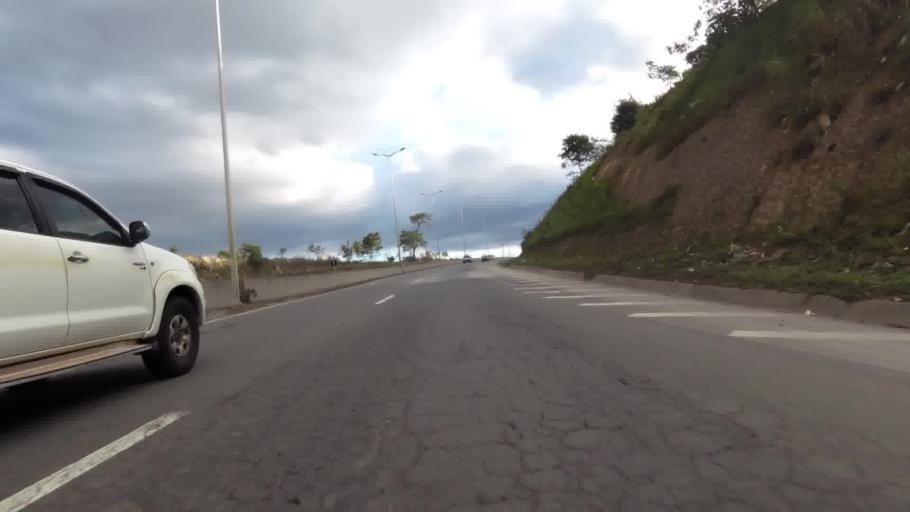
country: BR
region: Espirito Santo
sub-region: Vitoria
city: Vitoria
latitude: -20.2616
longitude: -40.3792
